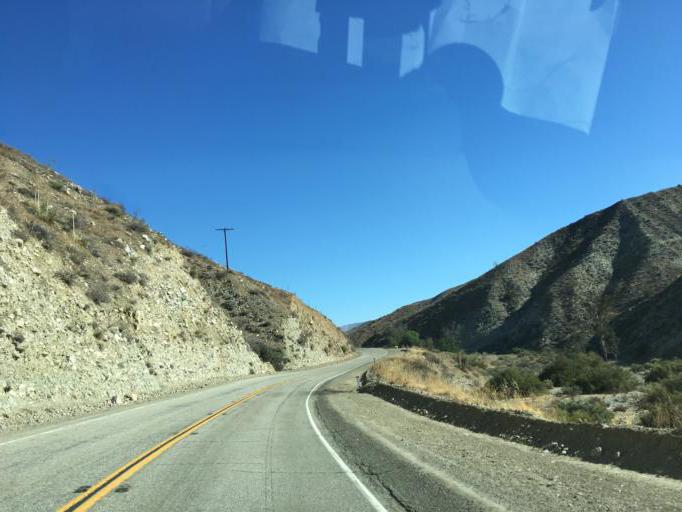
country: US
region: California
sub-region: Los Angeles County
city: Agua Dulce
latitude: 34.4414
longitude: -118.3337
